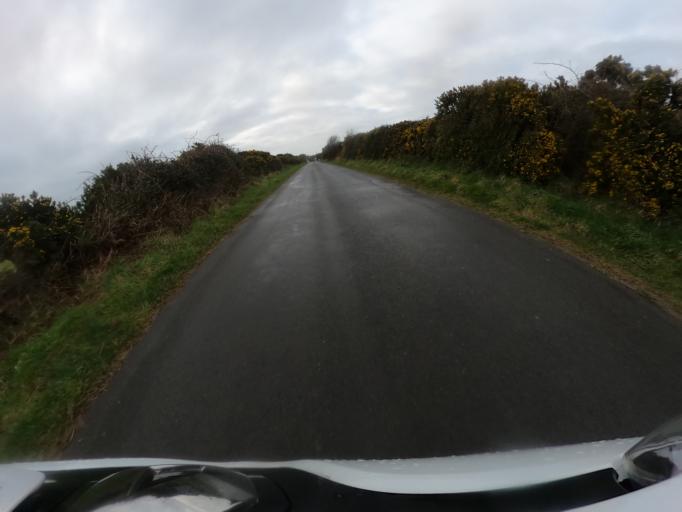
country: IM
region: Ramsey
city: Ramsey
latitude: 54.3528
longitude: -4.5318
